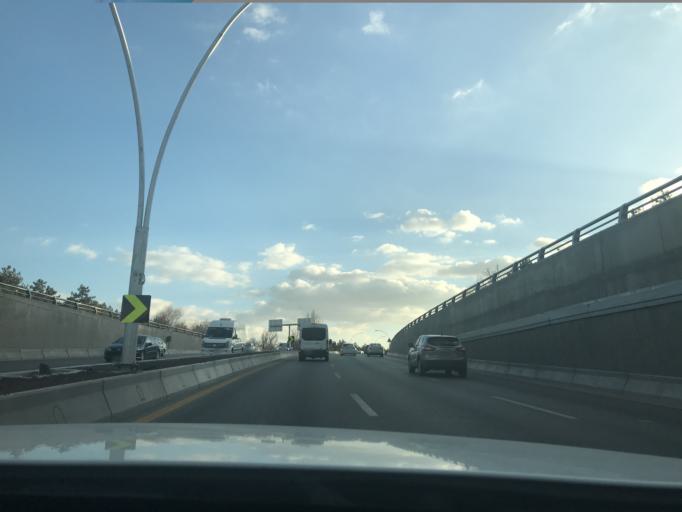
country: TR
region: Ankara
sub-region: Goelbasi
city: Golbasi
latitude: 39.8483
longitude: 32.8107
